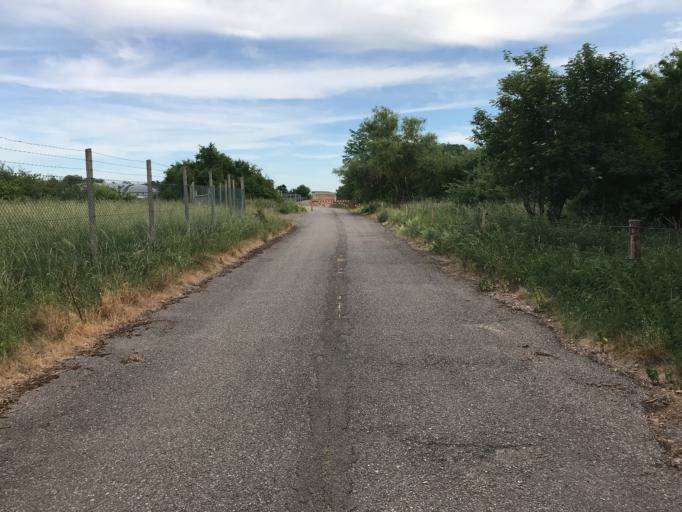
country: DK
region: Capital Region
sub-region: Ballerup Kommune
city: Malov
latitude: 55.7654
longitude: 12.3042
